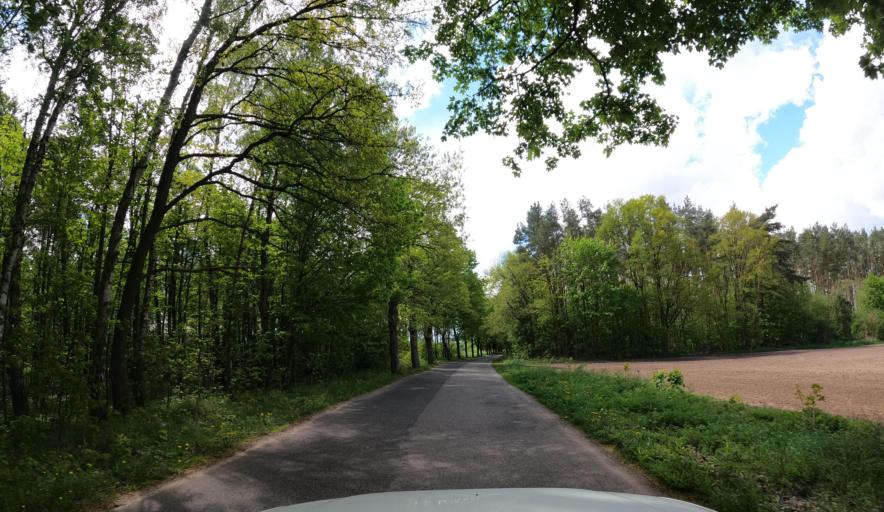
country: PL
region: West Pomeranian Voivodeship
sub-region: Powiat kamienski
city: Wolin
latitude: 53.8789
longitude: 14.6529
